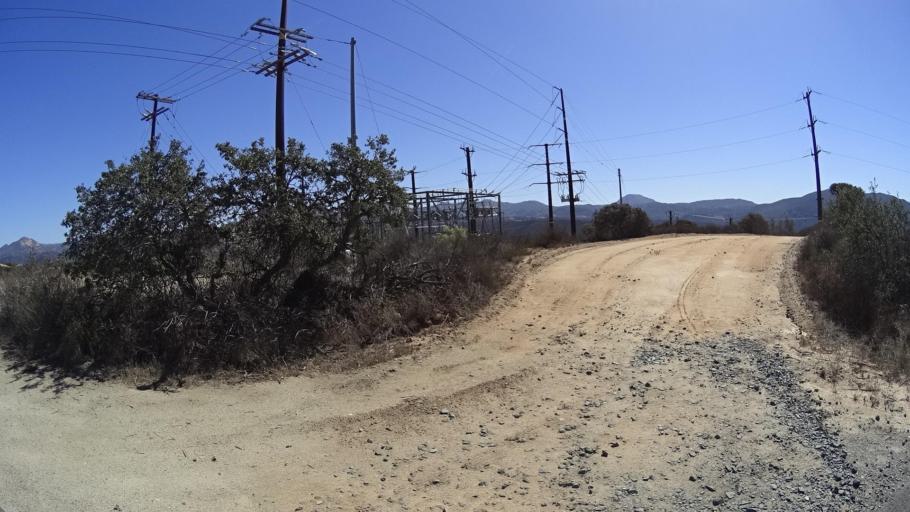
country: US
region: California
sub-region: San Diego County
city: Harbison Canyon
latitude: 32.7972
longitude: -116.7928
